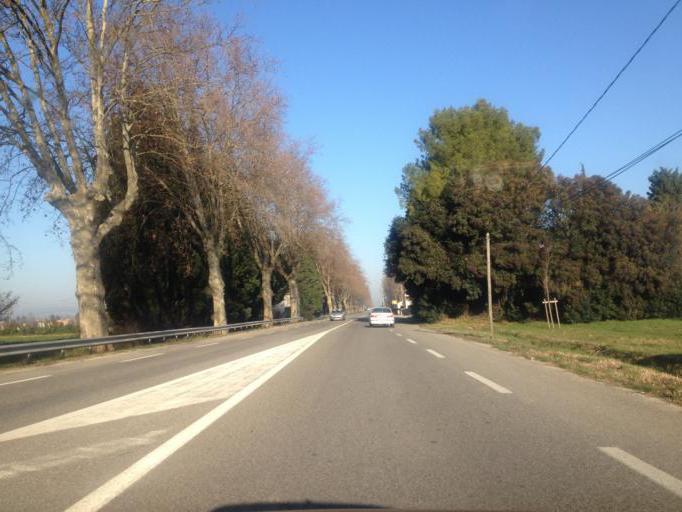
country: FR
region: Provence-Alpes-Cote d'Azur
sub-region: Departement du Vaucluse
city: Mondragon
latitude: 44.2609
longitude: 4.7054
